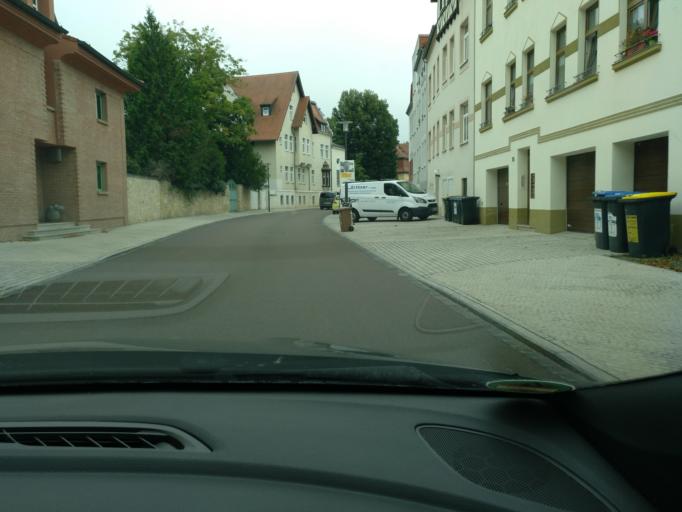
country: DE
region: Saxony-Anhalt
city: Sennewitz
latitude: 51.5056
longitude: 11.9543
